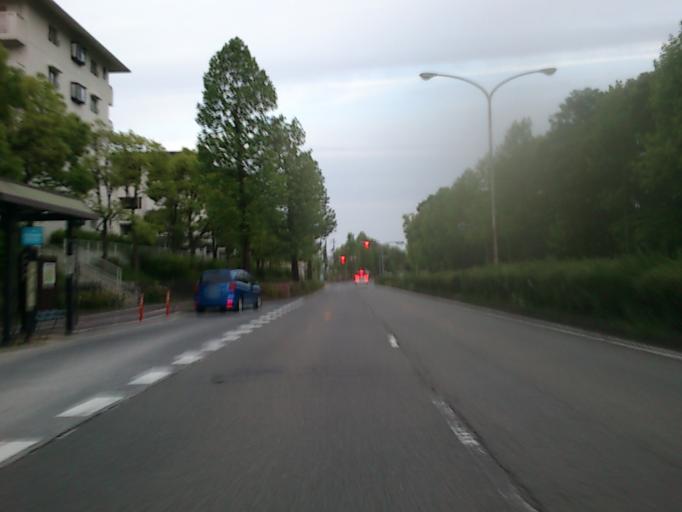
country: JP
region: Kyoto
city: Muko
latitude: 34.9606
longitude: 135.6796
